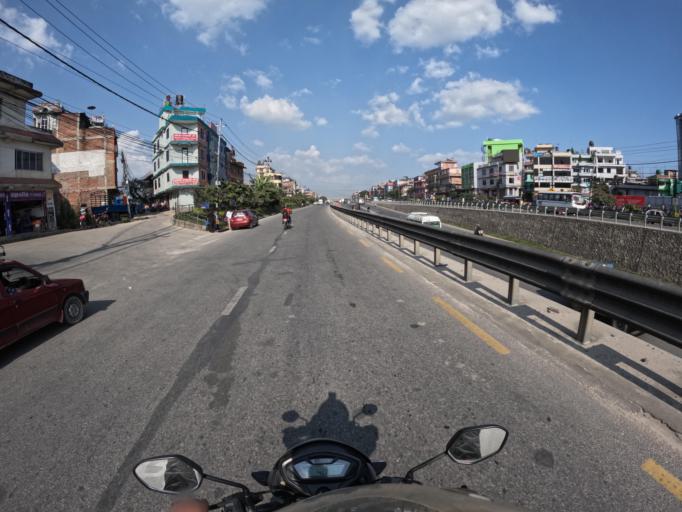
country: NP
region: Central Region
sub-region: Bagmati Zone
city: Patan
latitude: 27.6753
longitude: 85.3439
